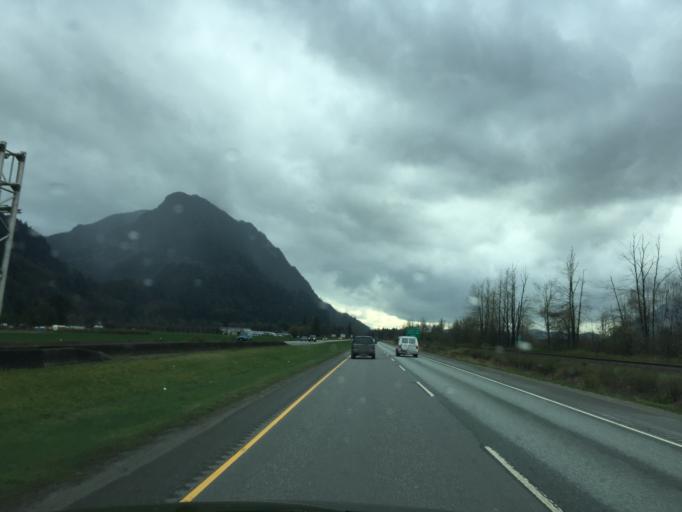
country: CA
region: British Columbia
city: Hope
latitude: 49.3287
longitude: -121.6144
